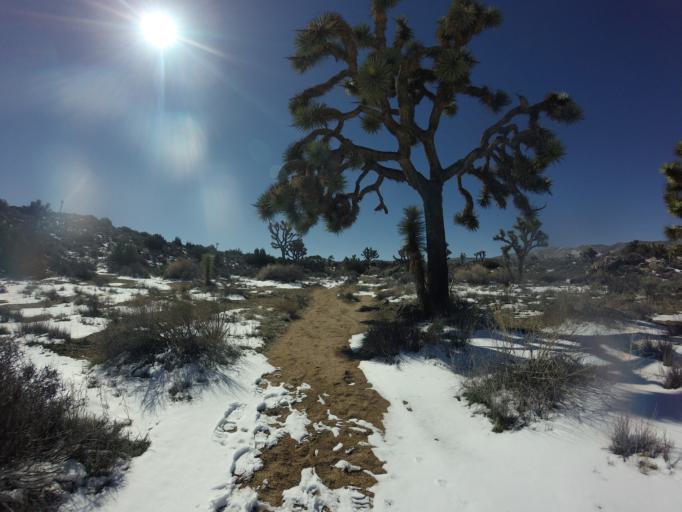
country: US
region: California
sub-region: Riverside County
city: Sky Valley
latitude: 33.9494
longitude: -116.1621
